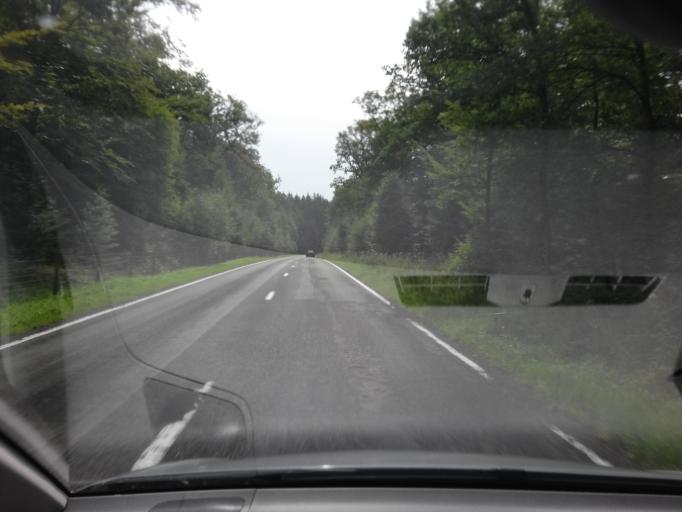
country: BE
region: Wallonia
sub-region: Province du Luxembourg
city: Chiny
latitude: 49.7720
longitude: 5.3575
